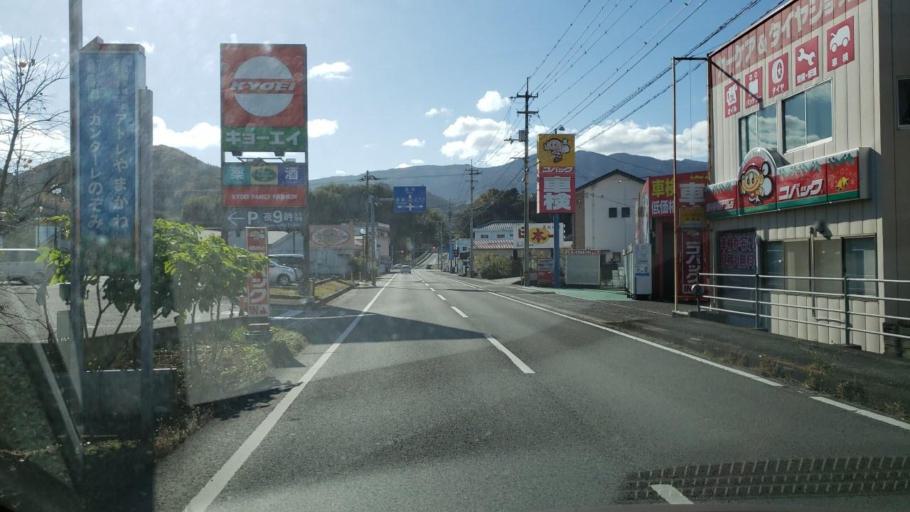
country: JP
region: Tokushima
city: Wakimachi
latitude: 34.0589
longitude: 134.2384
